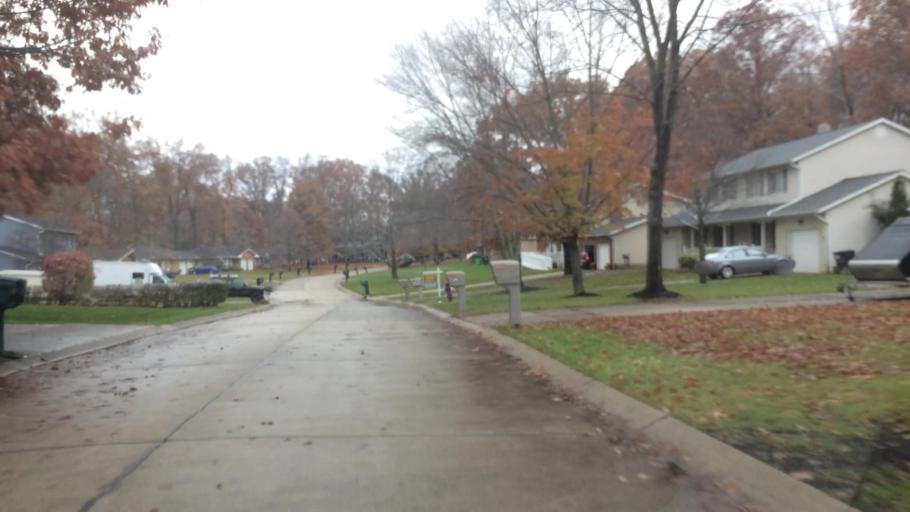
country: US
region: Ohio
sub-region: Summit County
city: Silver Lake
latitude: 41.1807
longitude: -81.4519
